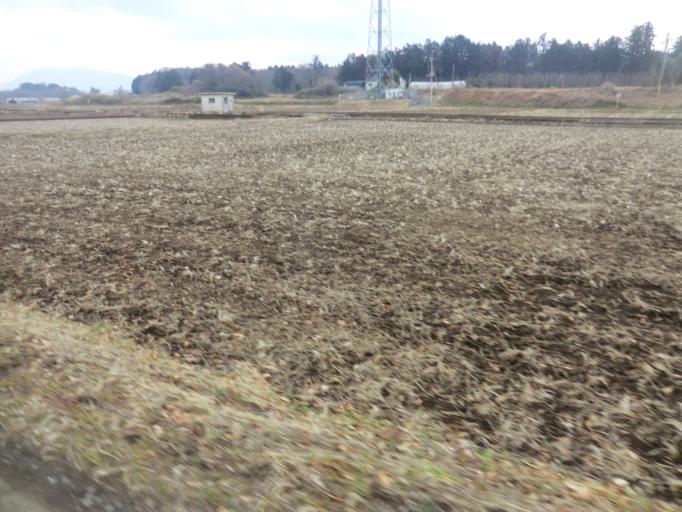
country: JP
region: Ibaraki
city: Naka
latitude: 36.1035
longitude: 140.1133
